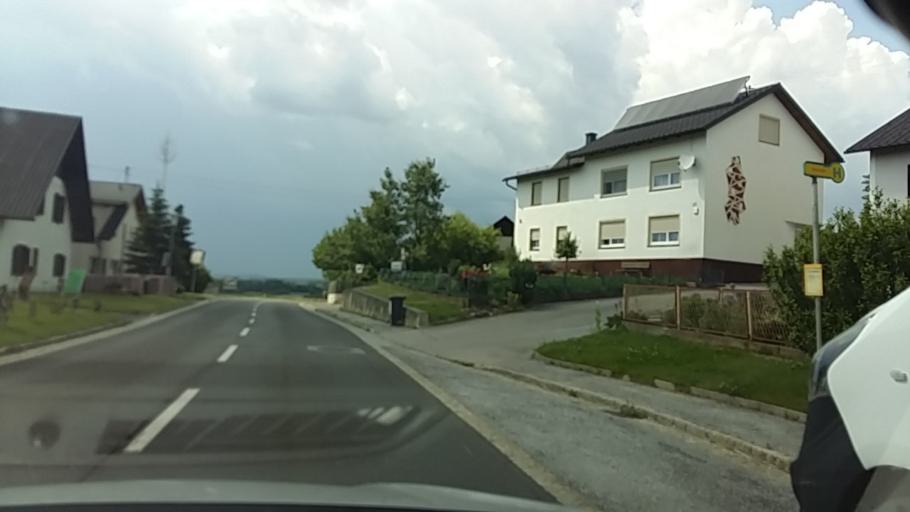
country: AT
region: Styria
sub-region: Politischer Bezirk Hartberg-Fuerstenfeld
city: Soechau
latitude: 47.0345
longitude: 16.0071
